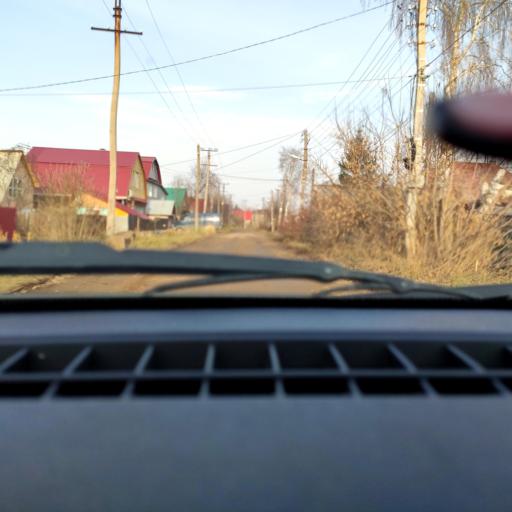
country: RU
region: Bashkortostan
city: Iglino
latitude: 54.8231
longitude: 56.1857
